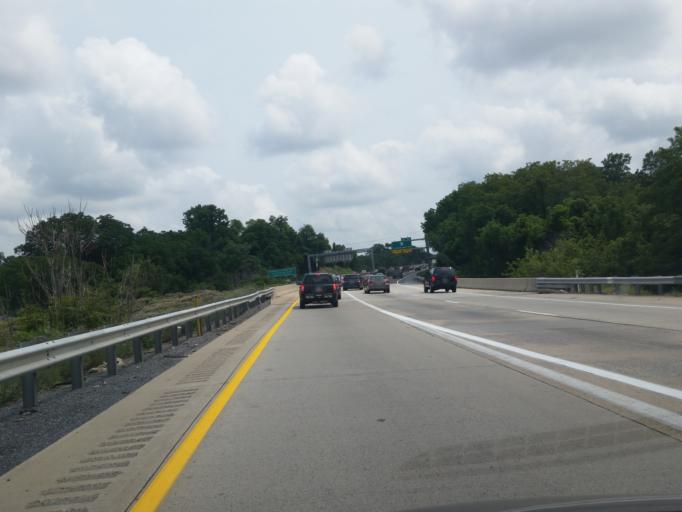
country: US
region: Pennsylvania
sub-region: Dauphin County
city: Progress
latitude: 40.3046
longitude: -76.8308
